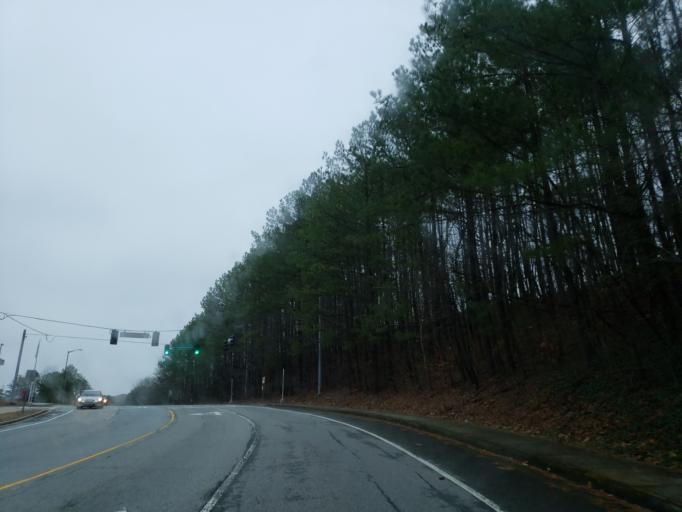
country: US
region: Georgia
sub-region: Fulton County
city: Roswell
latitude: 34.0157
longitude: -84.3233
